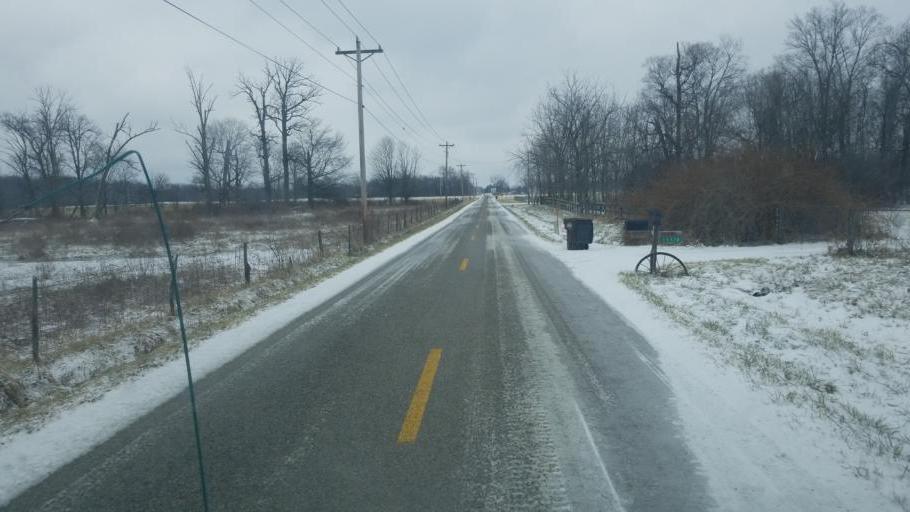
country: US
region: Ohio
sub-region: Knox County
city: Centerburg
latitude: 40.3090
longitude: -82.7764
